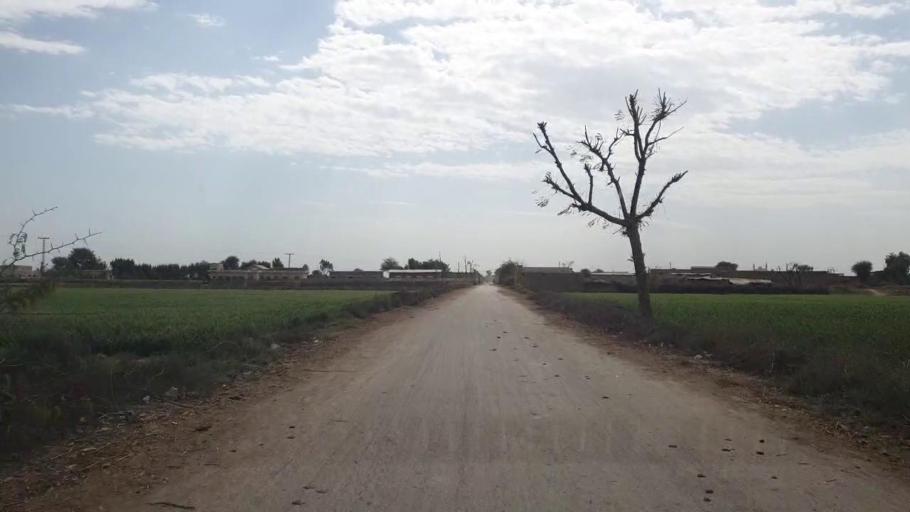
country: PK
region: Sindh
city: Hala
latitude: 25.9441
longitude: 68.4298
